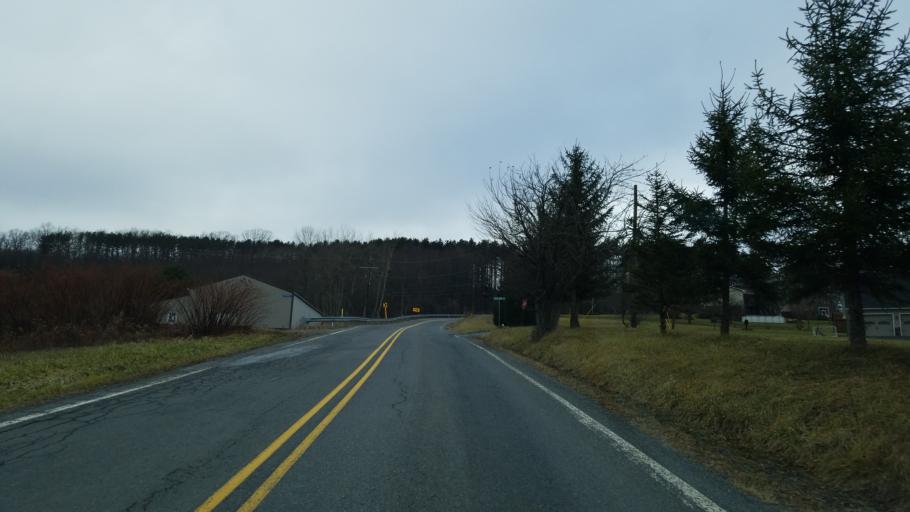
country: US
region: Pennsylvania
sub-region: Clearfield County
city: Hyde
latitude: 41.0375
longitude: -78.4895
